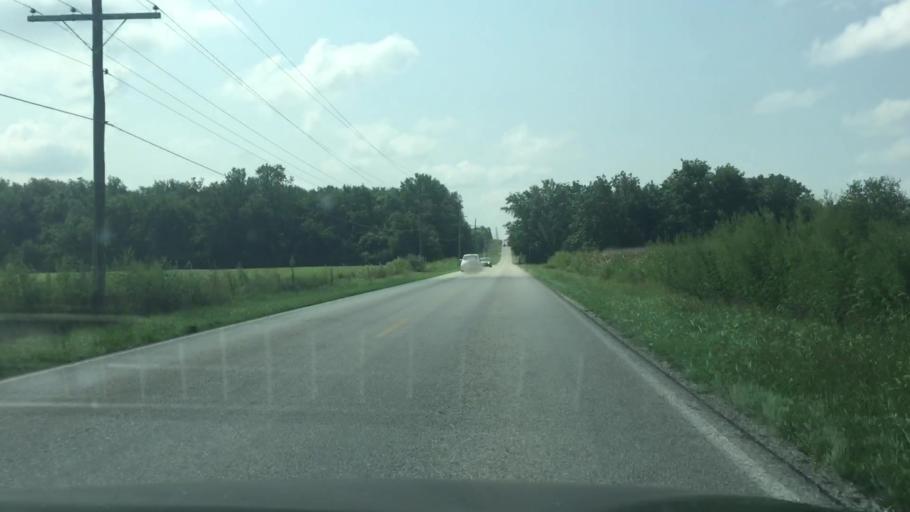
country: US
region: Kansas
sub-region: Allen County
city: Humboldt
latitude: 37.8691
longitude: -95.4369
